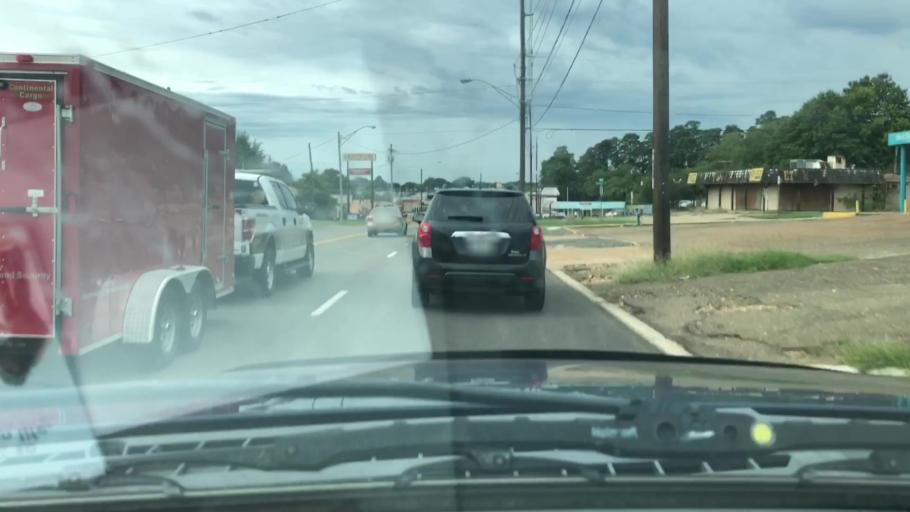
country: US
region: Texas
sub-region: Bowie County
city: Texarkana
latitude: 33.4351
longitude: -94.0712
